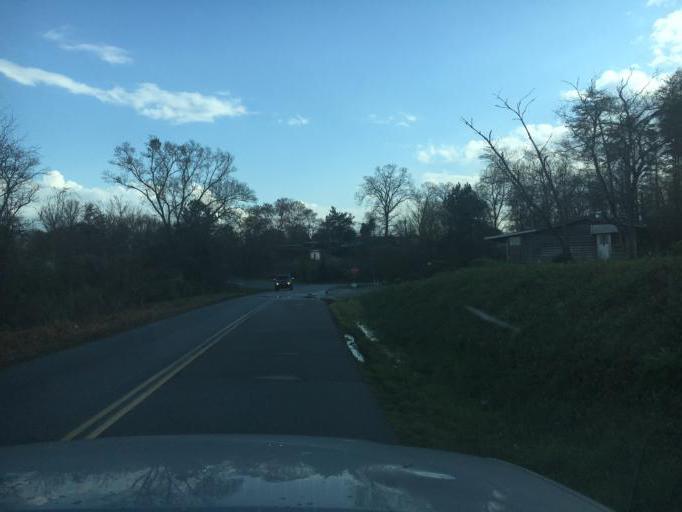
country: US
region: South Carolina
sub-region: Greenville County
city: Parker
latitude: 34.8575
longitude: -82.5021
